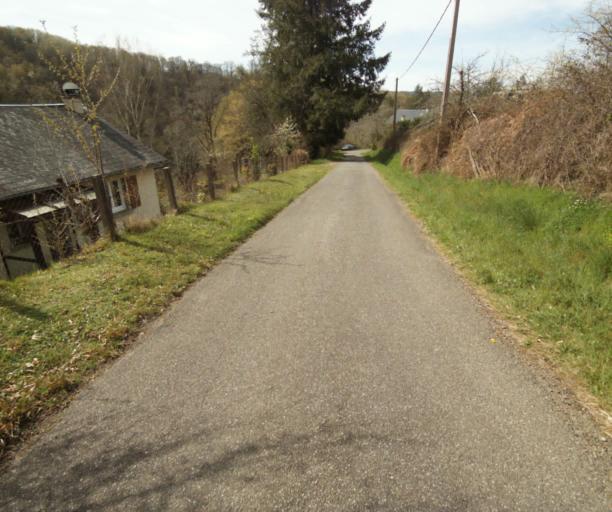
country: FR
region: Limousin
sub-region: Departement de la Correze
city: Laguenne
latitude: 45.2505
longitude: 1.8217
